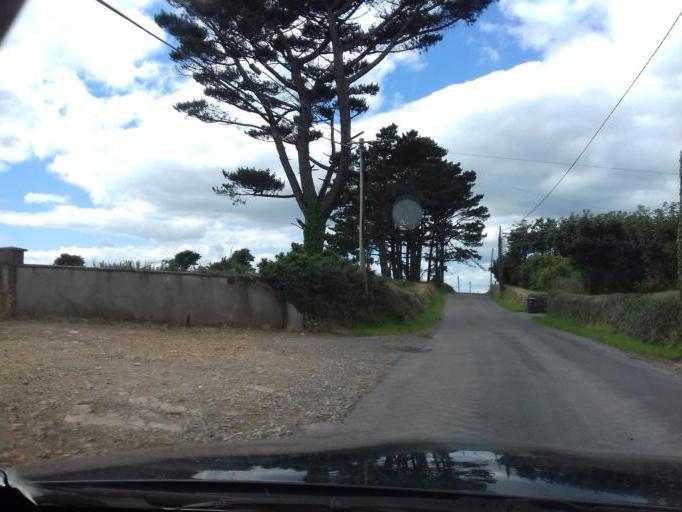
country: IE
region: Leinster
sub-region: Kilkenny
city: Mooncoin
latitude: 52.1737
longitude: -7.2723
